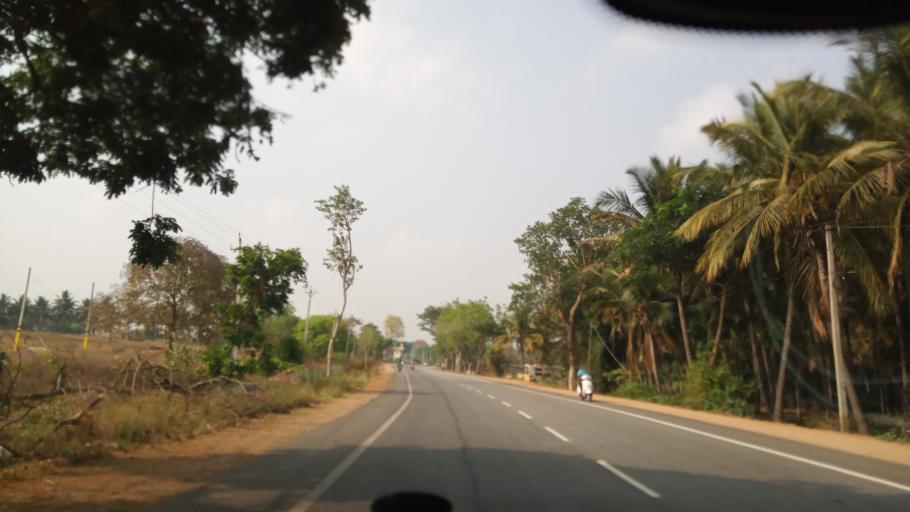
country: IN
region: Karnataka
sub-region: Mandya
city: Nagamangala
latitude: 12.8055
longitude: 76.7526
